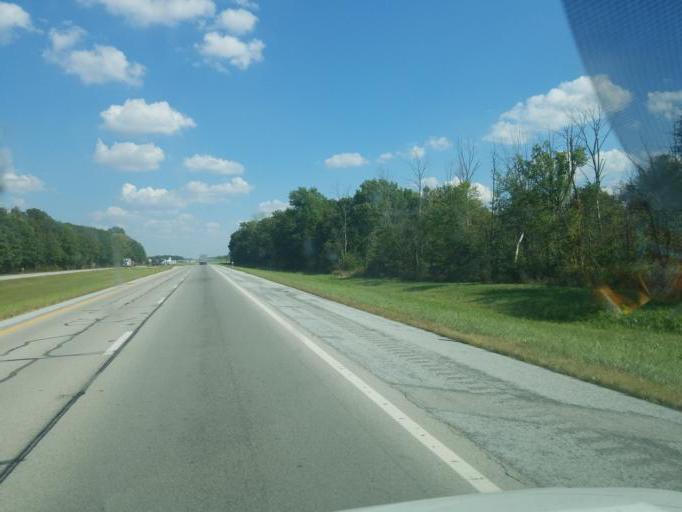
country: US
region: Ohio
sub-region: Allen County
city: Lima
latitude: 40.8240
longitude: -84.1091
